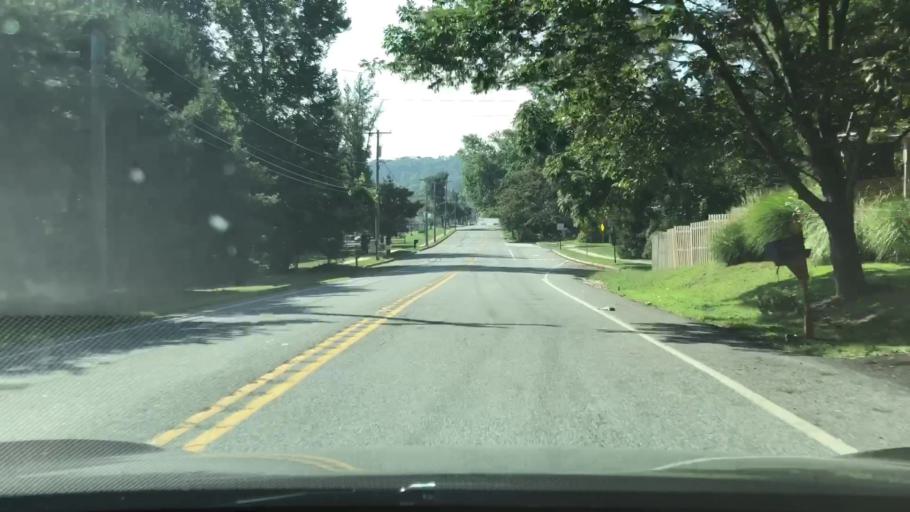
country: US
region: Pennsylvania
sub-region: Montgomery County
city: Dresher
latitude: 40.1471
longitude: -75.1695
